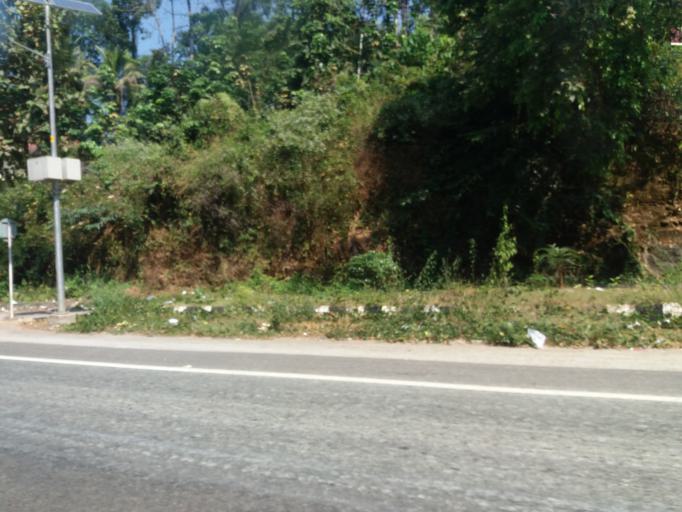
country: IN
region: Kerala
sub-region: Ernakulam
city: Muvattupuzha
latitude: 9.8844
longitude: 76.6969
